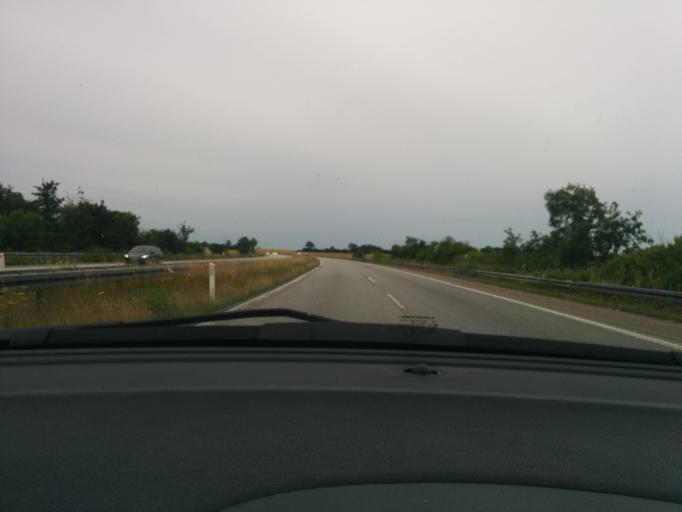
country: DK
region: Zealand
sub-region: Faxe Kommune
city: Haslev
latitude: 55.3418
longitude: 12.0461
